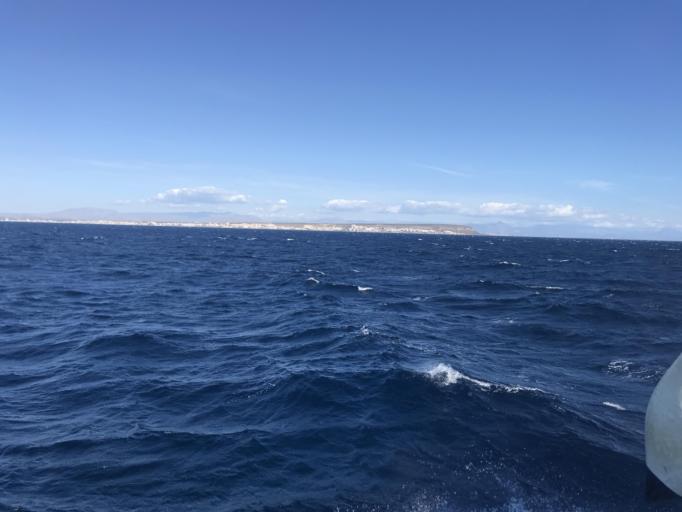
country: ES
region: Valencia
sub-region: Provincia de Alicante
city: Santa Pola
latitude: 38.1333
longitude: -0.5332
